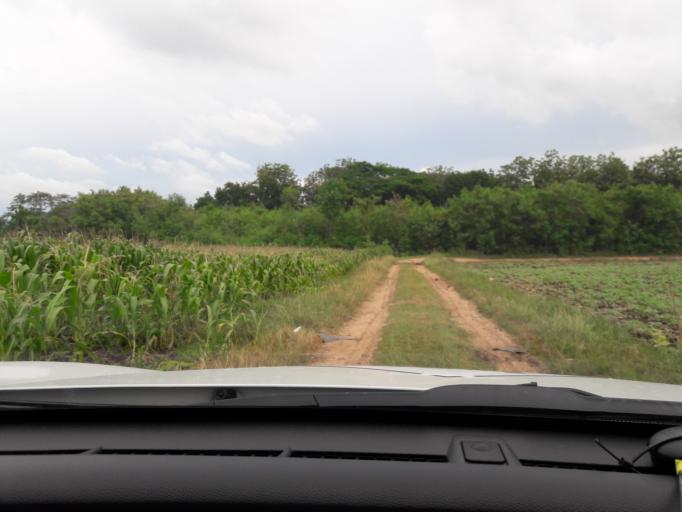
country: TH
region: Nakhon Sawan
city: Tak Fa
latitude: 15.3418
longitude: 100.5037
